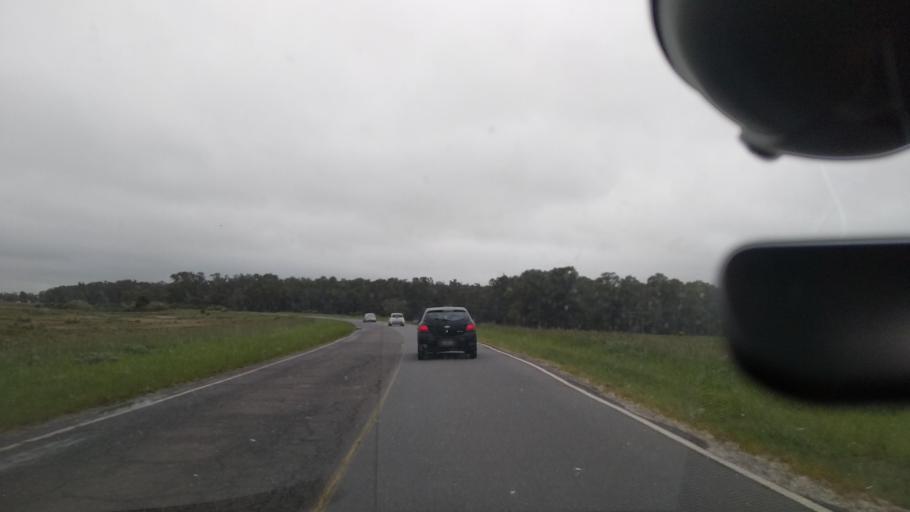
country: AR
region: Buenos Aires
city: Veronica
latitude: -35.4696
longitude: -57.3240
